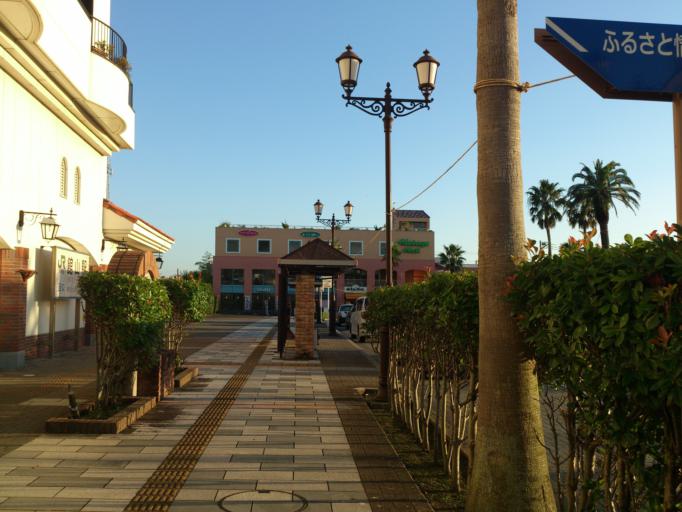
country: JP
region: Chiba
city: Tateyama
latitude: 34.9958
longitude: 139.8616
